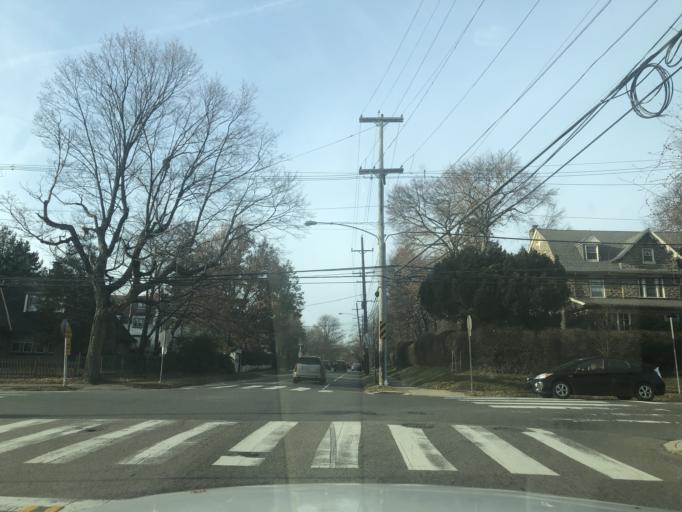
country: US
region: Pennsylvania
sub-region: Montgomery County
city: Bala-Cynwyd
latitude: 40.0185
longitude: -75.1829
